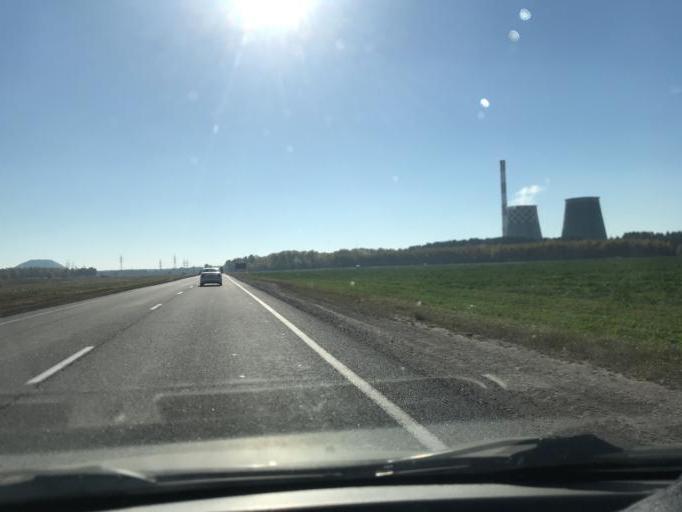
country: BY
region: Gomel
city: Kastsyukowka
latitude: 52.4584
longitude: 30.8247
